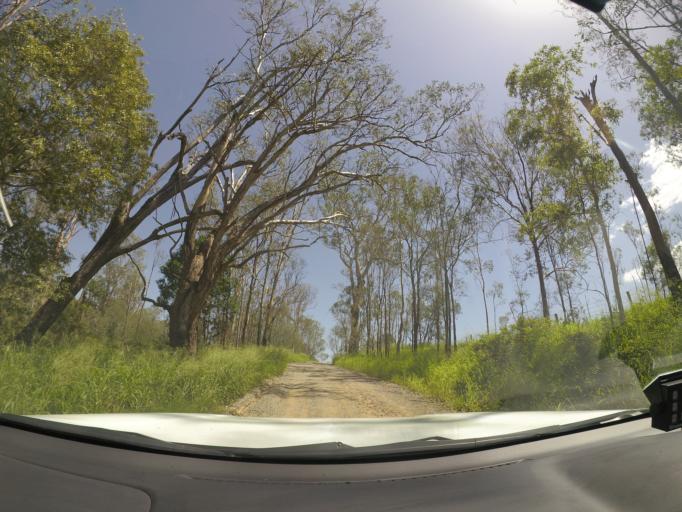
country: AU
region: Queensland
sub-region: Logan
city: North Maclean
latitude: -27.8370
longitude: 152.8712
